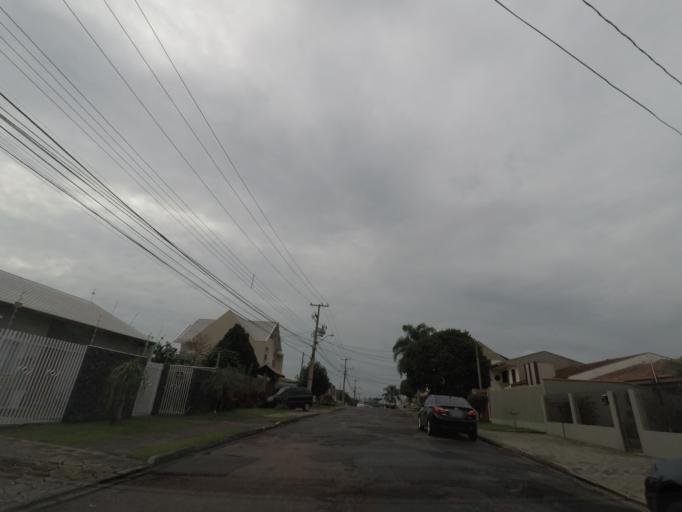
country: BR
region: Parana
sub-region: Curitiba
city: Curitiba
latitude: -25.4720
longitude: -49.3113
